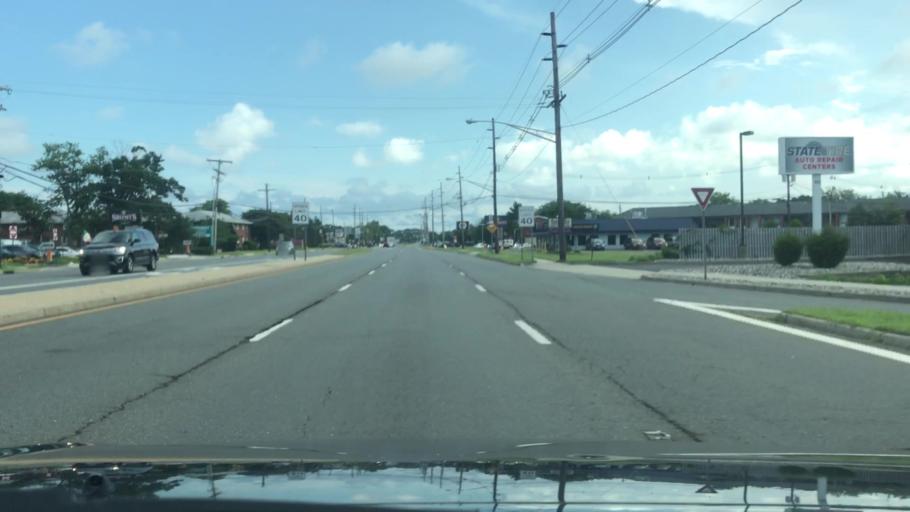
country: US
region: New Jersey
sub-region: Ocean County
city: Leisure Village East
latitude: 40.0485
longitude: -74.1423
